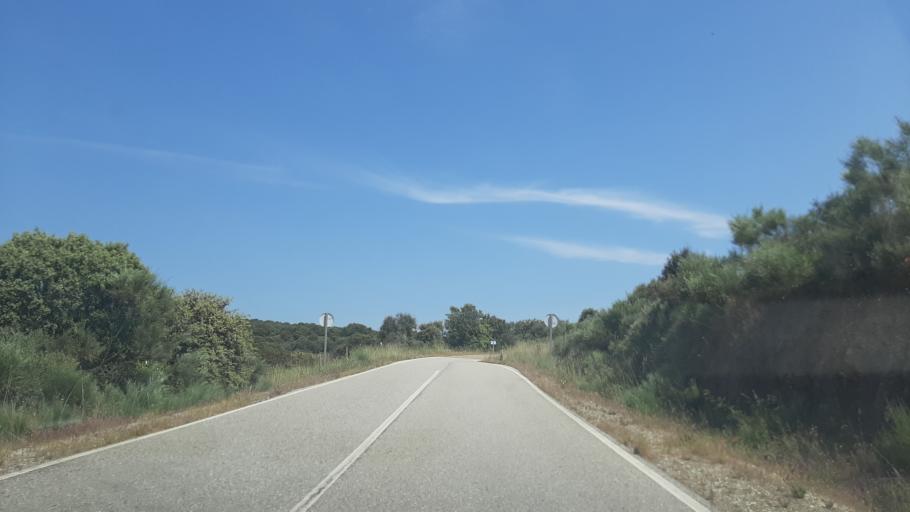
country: ES
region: Castille and Leon
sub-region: Provincia de Salamanca
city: Aldea del Obispo
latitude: 40.6537
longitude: -6.7771
